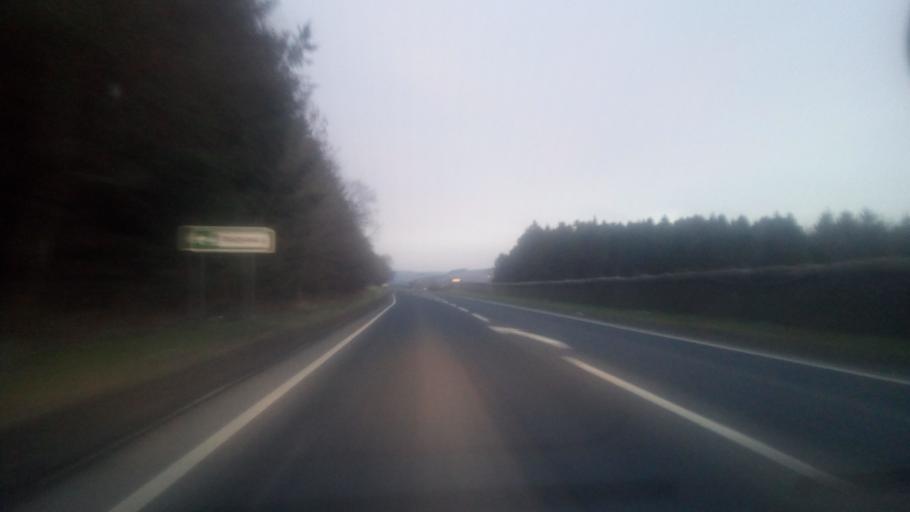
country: GB
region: Scotland
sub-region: The Scottish Borders
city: Lauder
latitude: 55.7339
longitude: -2.7652
